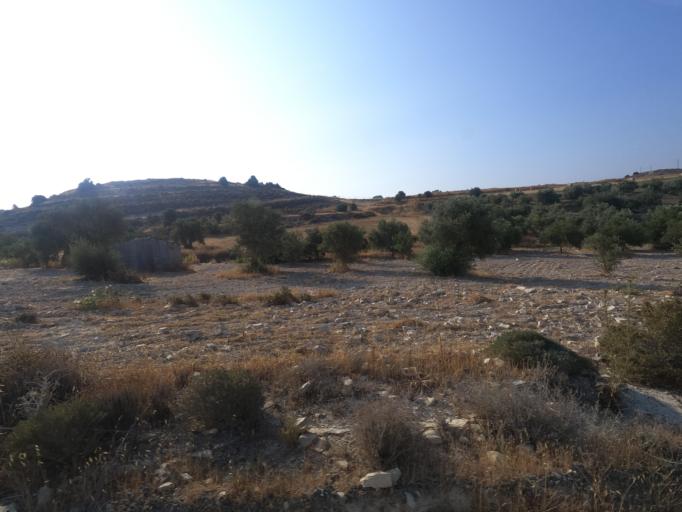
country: CY
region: Larnaka
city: Psevdas
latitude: 34.9372
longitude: 33.5030
